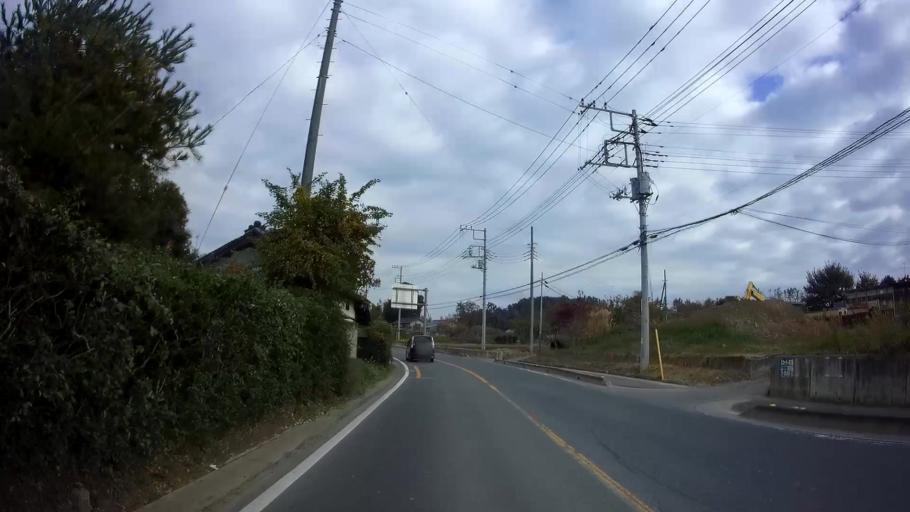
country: JP
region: Saitama
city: Okegawa
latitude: 36.0066
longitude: 139.5186
